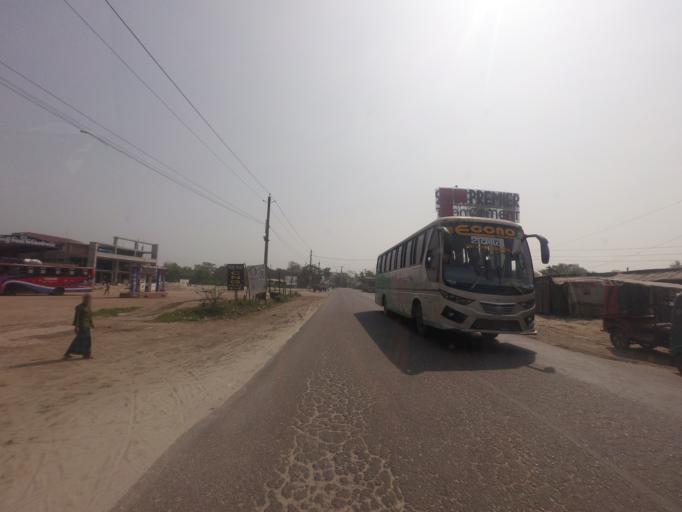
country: BD
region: Dhaka
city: Bhairab Bazar
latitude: 24.0562
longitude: 90.9733
